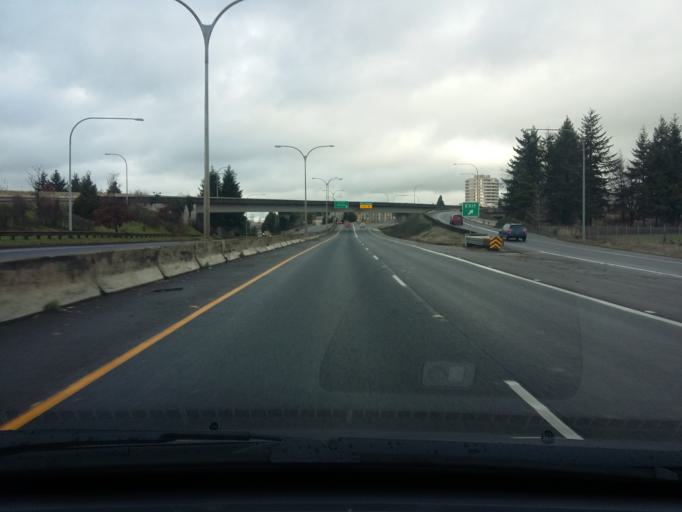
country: US
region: Washington
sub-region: Clark County
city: Vancouver
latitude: 45.6213
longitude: -122.6678
